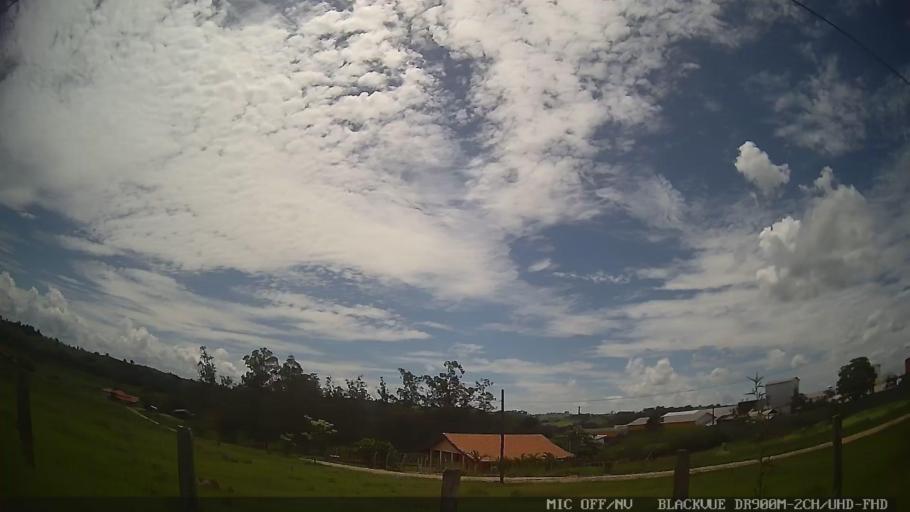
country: BR
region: Sao Paulo
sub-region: Conchas
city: Conchas
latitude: -23.0881
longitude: -47.9813
